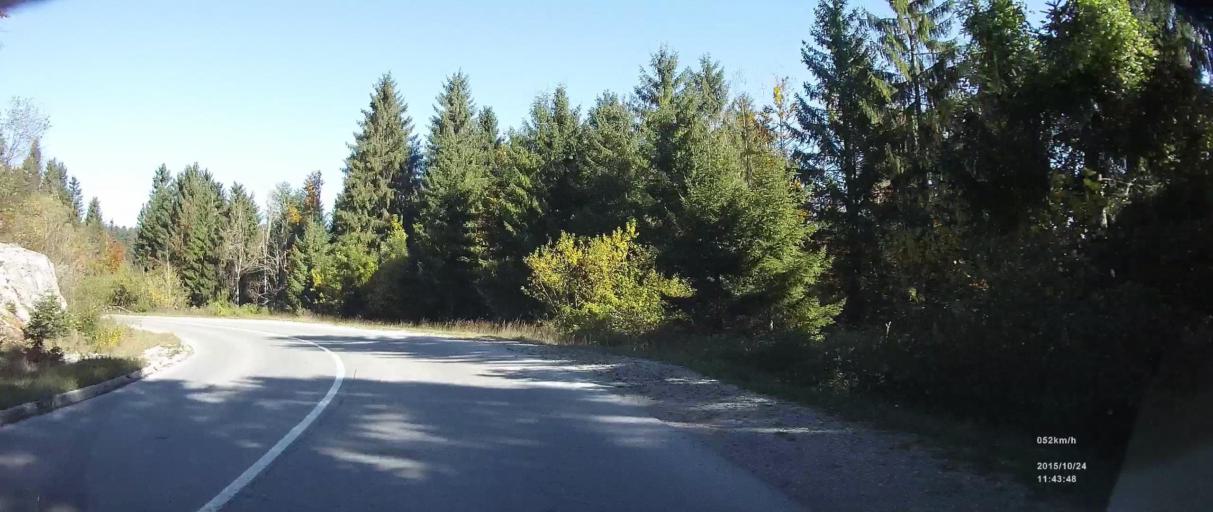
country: SI
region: Osilnica
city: Osilnica
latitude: 45.4354
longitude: 14.7089
